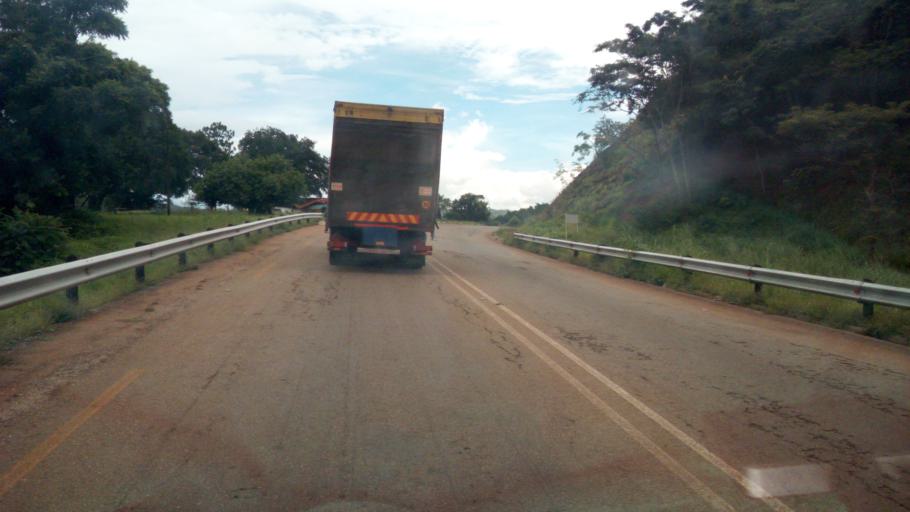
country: ZW
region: Mashonaland Central
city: Mazowe
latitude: -17.5213
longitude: 30.9872
